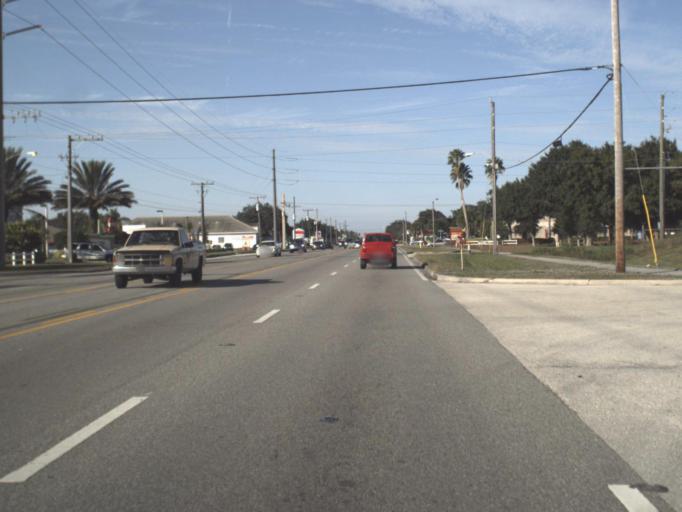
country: US
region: Florida
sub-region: Brevard County
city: June Park
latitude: 28.1415
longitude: -80.6717
